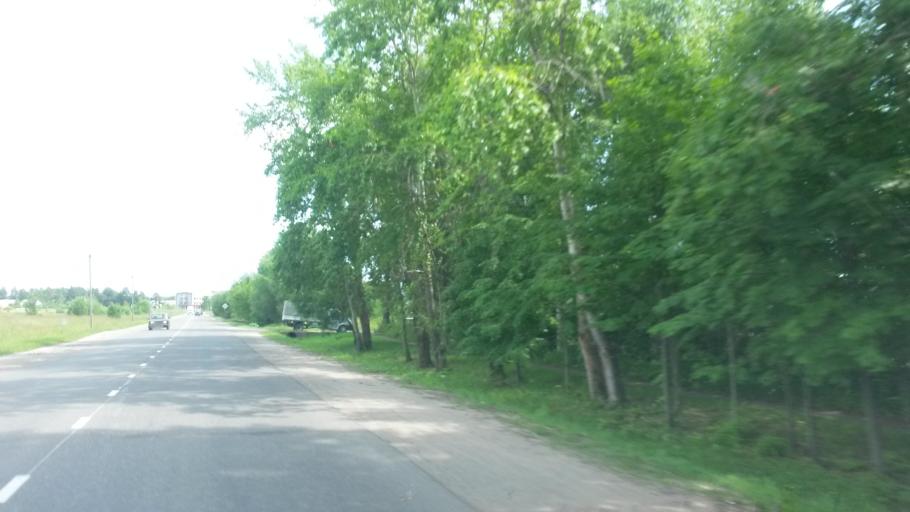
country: RU
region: Ivanovo
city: Zavolzhsk
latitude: 57.4986
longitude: 42.1255
